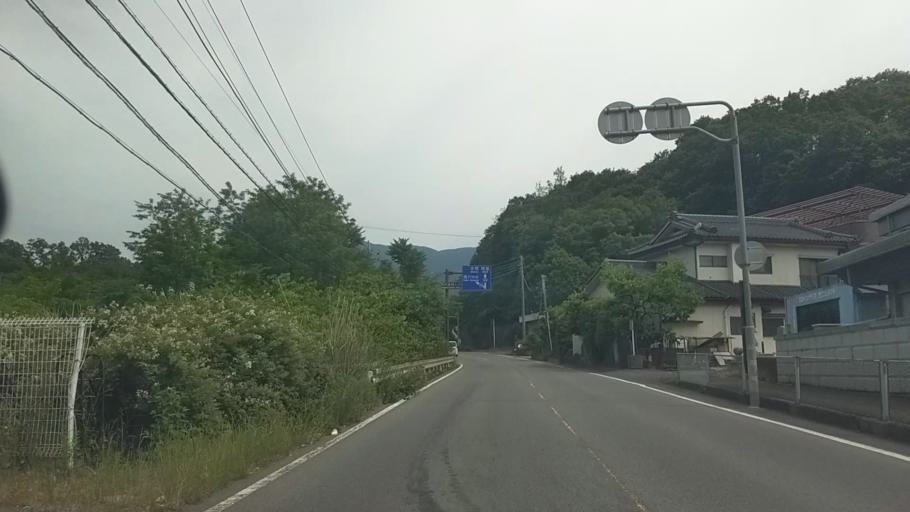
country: JP
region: Yamanashi
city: Isawa
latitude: 35.5934
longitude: 138.5886
